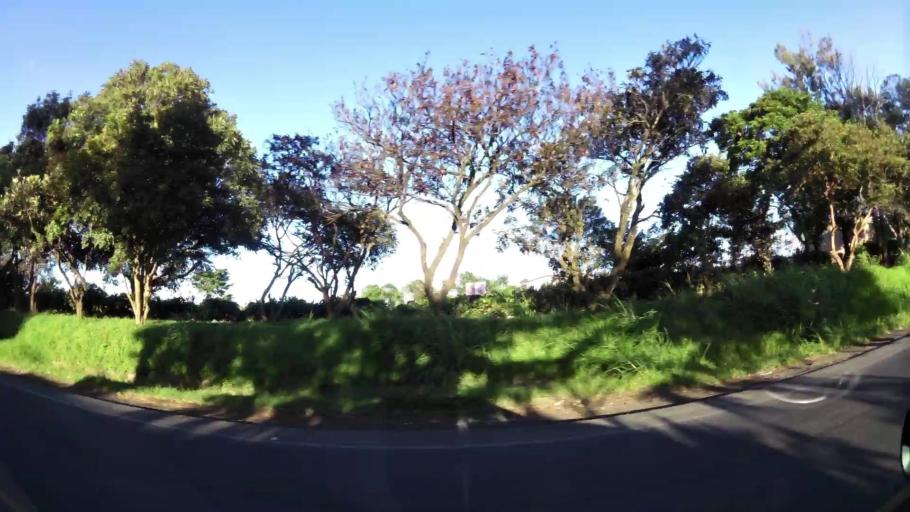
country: CR
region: Heredia
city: Angeles
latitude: 9.9856
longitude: -84.0456
